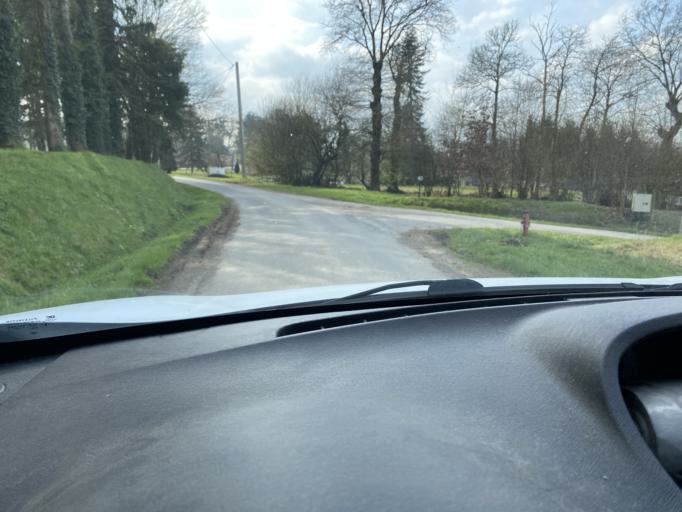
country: FR
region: Brittany
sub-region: Departement d'Ille-et-Vilaine
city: Melesse
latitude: 48.2255
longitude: -1.6646
